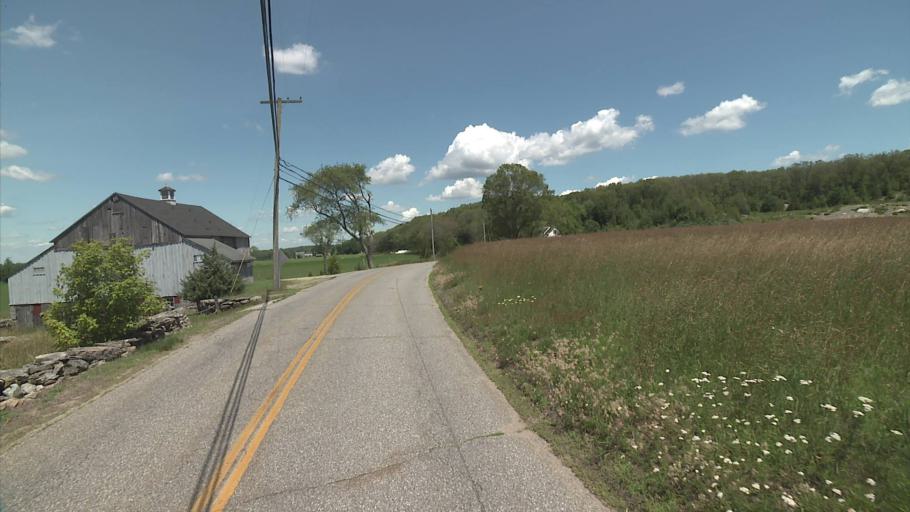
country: US
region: Connecticut
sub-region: New London County
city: Preston City
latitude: 41.5452
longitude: -71.8831
